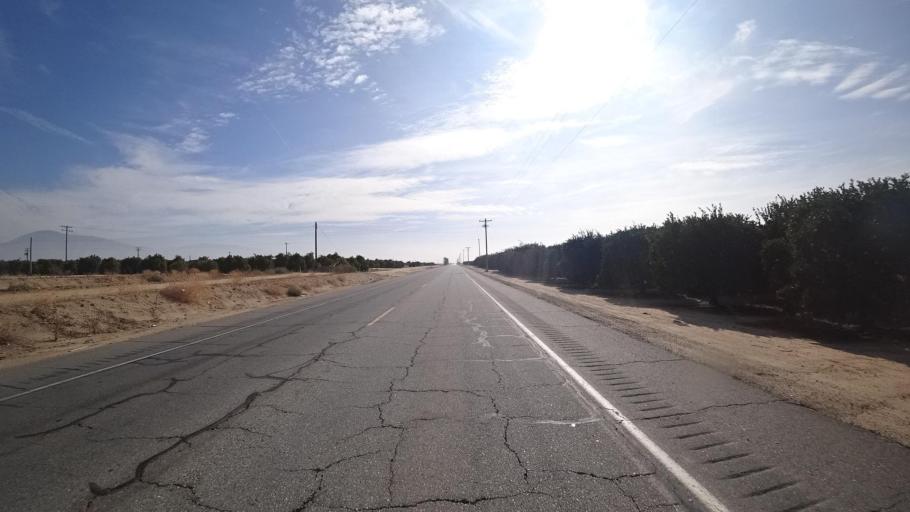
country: US
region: California
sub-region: Kern County
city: Lamont
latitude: 35.3191
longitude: -118.8431
